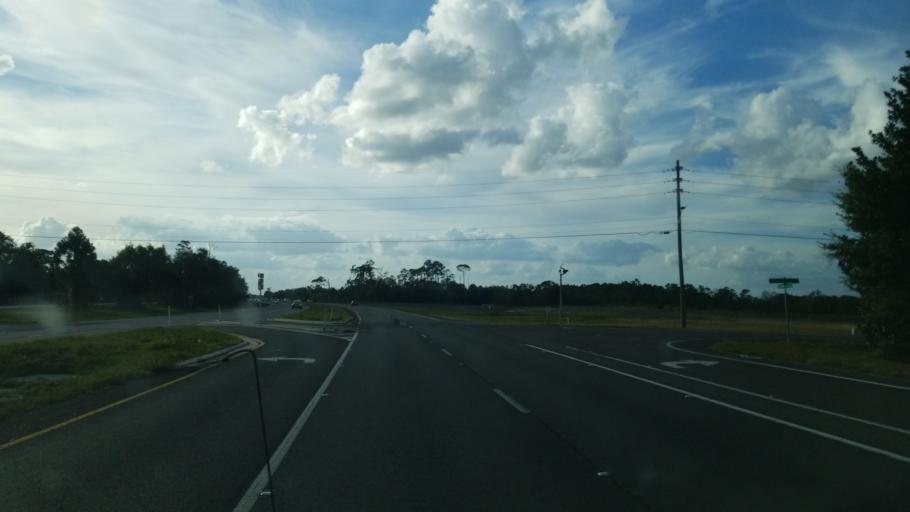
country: US
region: Florida
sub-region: Osceola County
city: Saint Cloud
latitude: 28.2412
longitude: -81.2017
